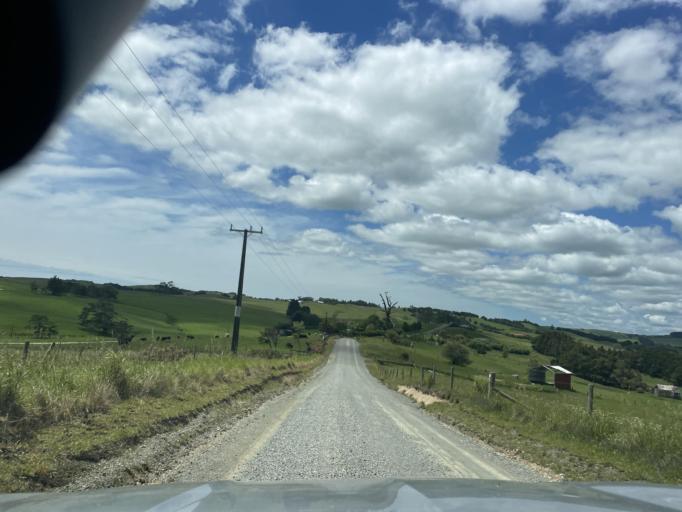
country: NZ
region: Auckland
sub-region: Auckland
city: Wellsford
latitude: -36.1504
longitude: 174.5171
